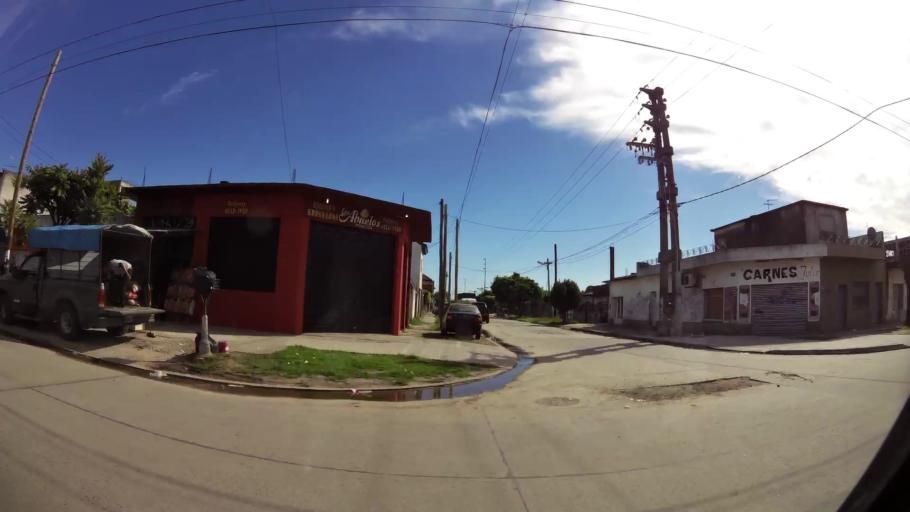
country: AR
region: Buenos Aires
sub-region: Partido de Almirante Brown
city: Adrogue
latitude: -34.7741
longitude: -58.3118
